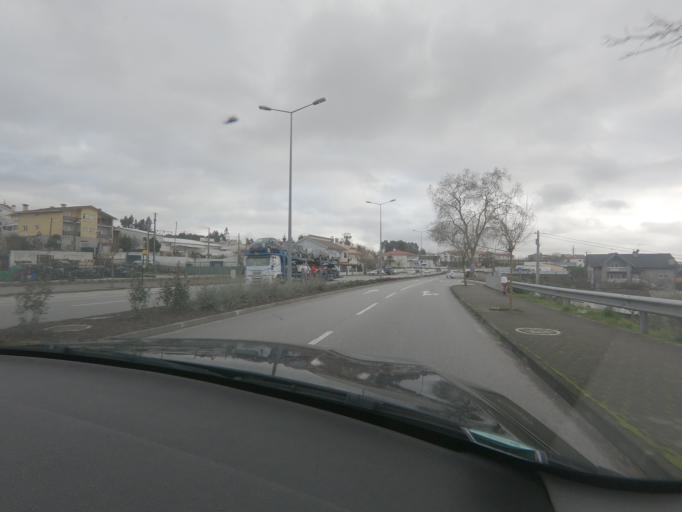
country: PT
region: Viseu
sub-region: Viseu
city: Abraveses
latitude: 40.6923
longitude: -7.9286
